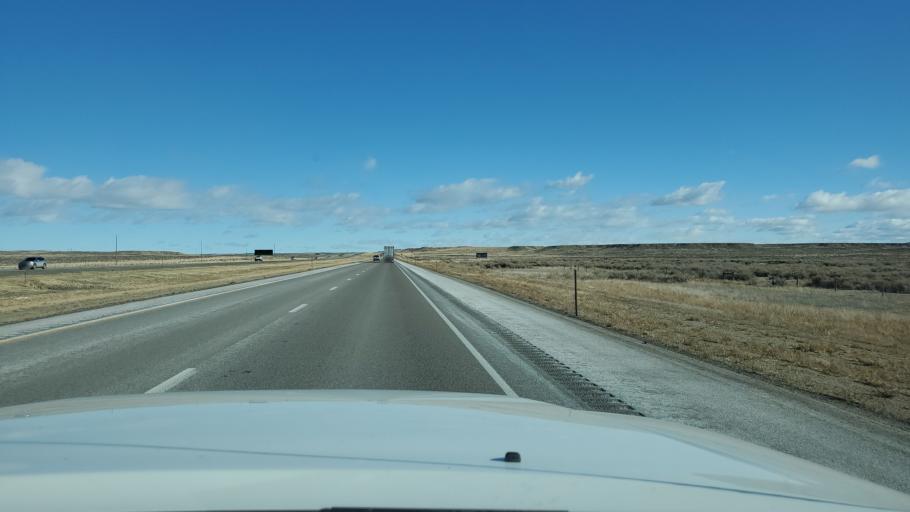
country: US
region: Wyoming
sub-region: Sweetwater County
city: Green River
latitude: 41.5429
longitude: -109.6646
